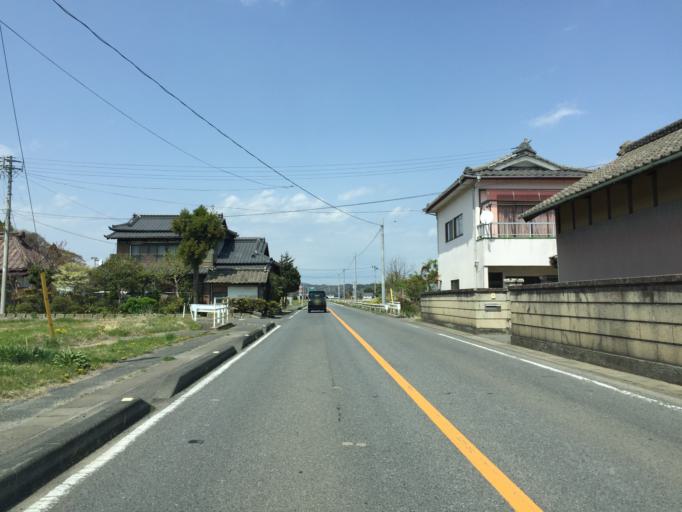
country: JP
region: Fukushima
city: Iwaki
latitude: 37.0999
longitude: 140.9537
